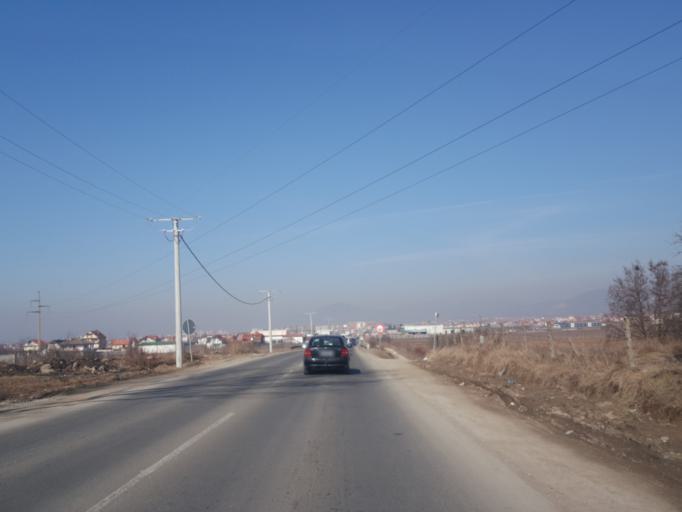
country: XK
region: Mitrovica
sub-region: Vushtrri
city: Vushtrri
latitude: 42.8023
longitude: 20.9937
